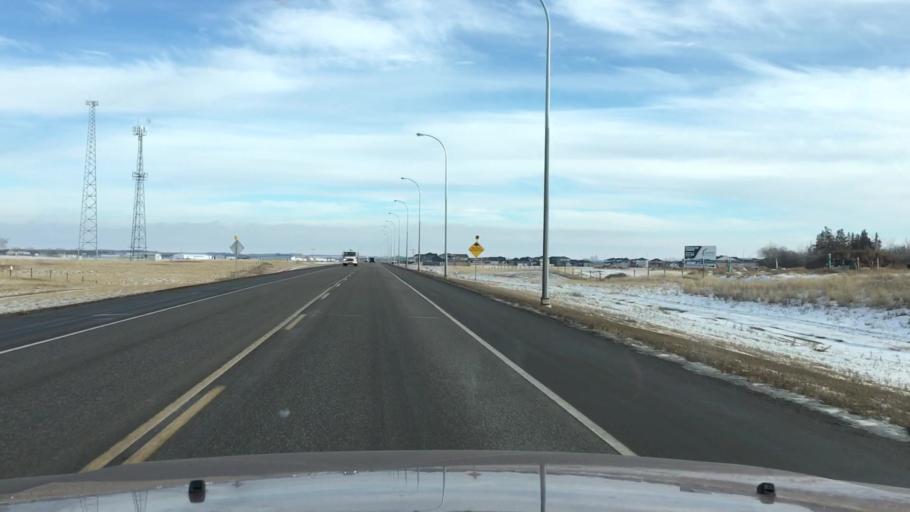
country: CA
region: Saskatchewan
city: Pilot Butte
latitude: 50.4865
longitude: -104.4285
